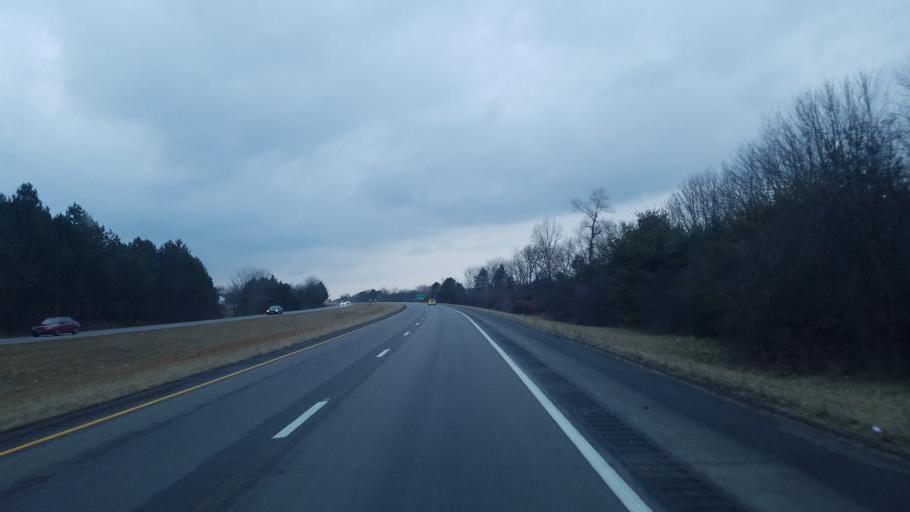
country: US
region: Ohio
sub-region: Wayne County
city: Dalton
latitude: 40.7863
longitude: -81.6164
